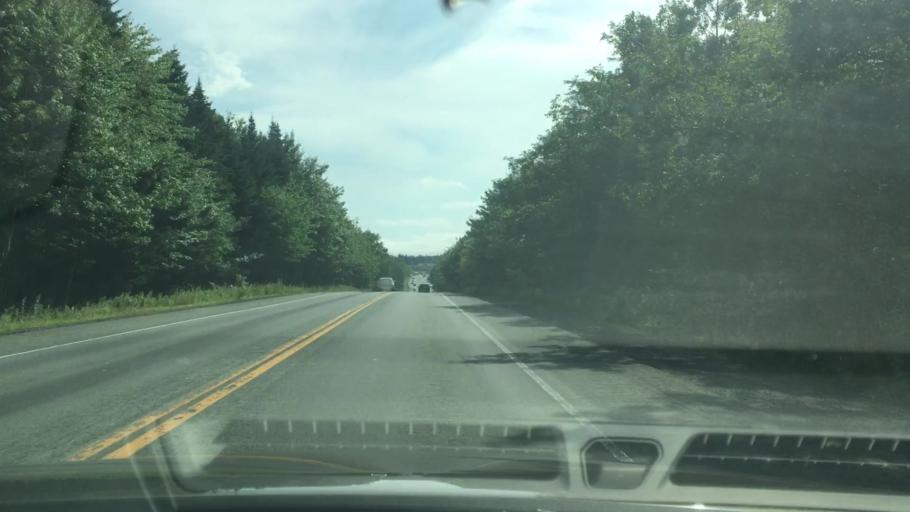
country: CA
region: Nova Scotia
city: Dartmouth
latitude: 44.7089
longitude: -63.8457
